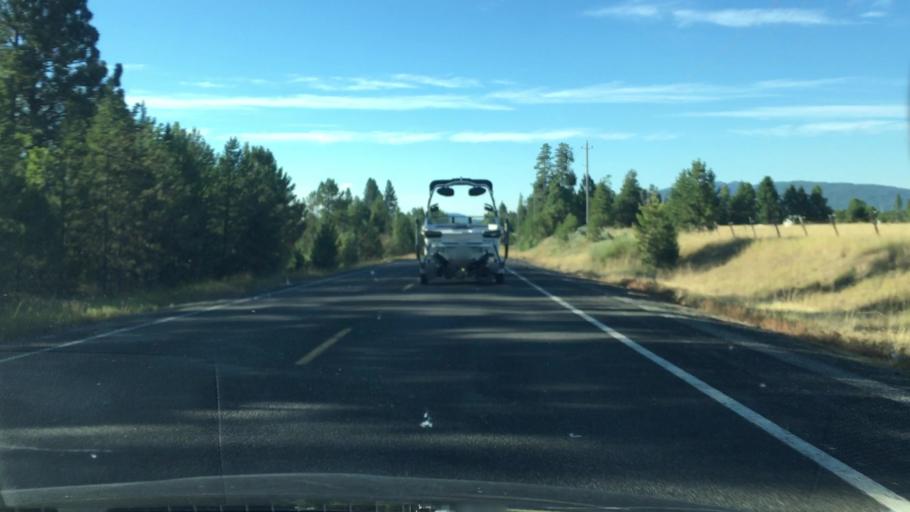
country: US
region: Idaho
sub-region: Valley County
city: Cascade
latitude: 44.4603
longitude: -115.9992
